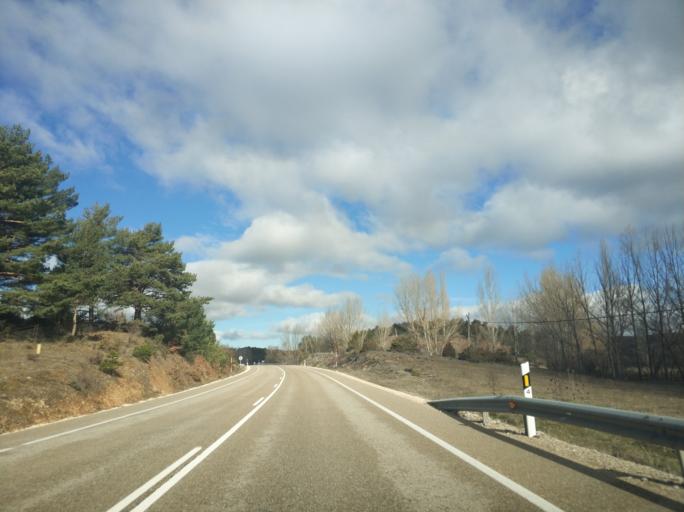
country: ES
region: Castille and Leon
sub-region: Provincia de Burgos
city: Rabanera del Pinar
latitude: 41.8676
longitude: -3.2113
